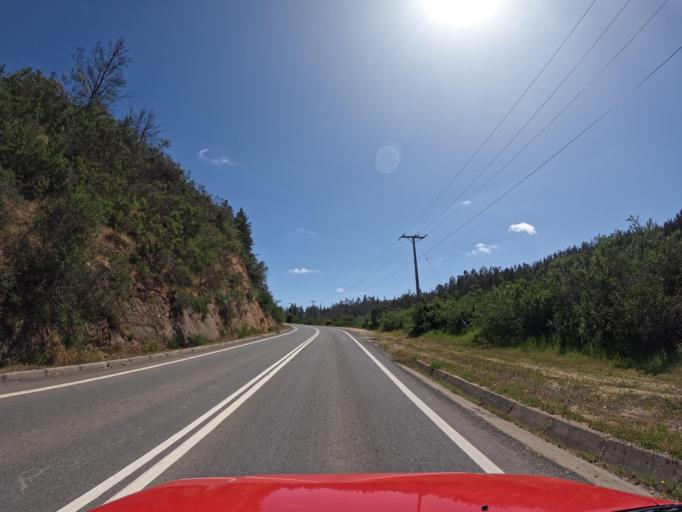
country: CL
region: O'Higgins
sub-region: Provincia de Colchagua
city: Santa Cruz
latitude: -34.6860
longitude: -71.7863
